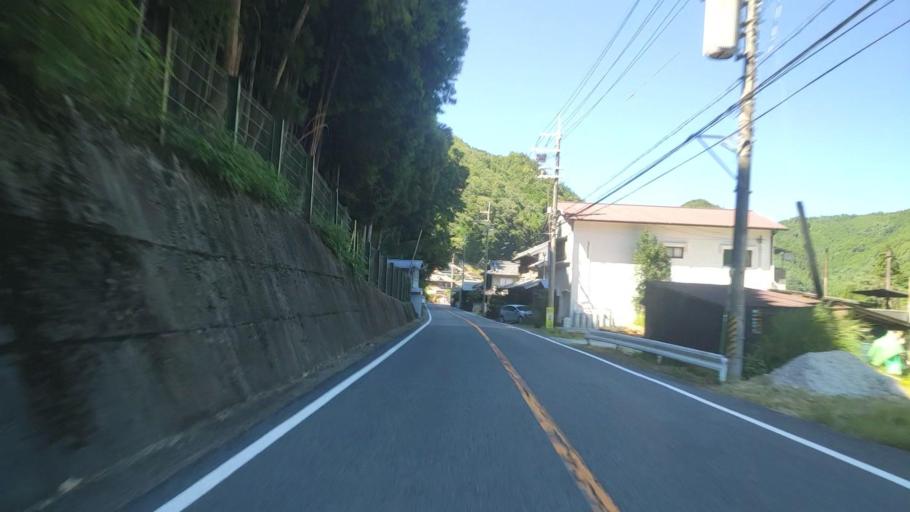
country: JP
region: Nara
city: Yoshino-cho
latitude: 34.3846
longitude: 135.9157
